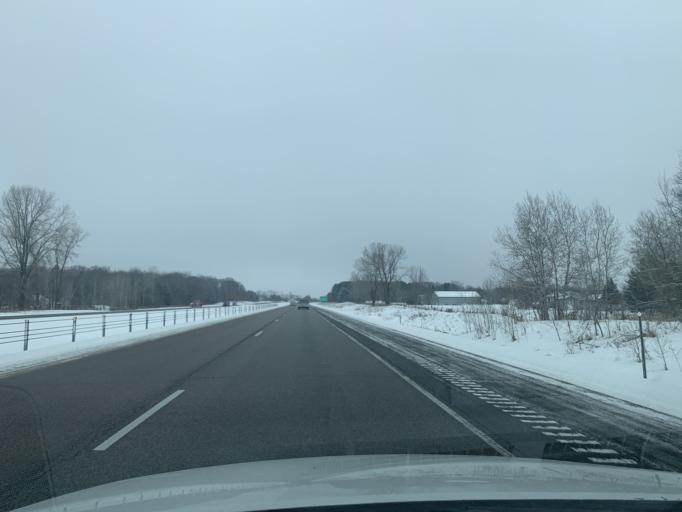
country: US
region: Minnesota
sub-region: Chisago County
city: North Branch
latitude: 45.4842
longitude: -92.9966
